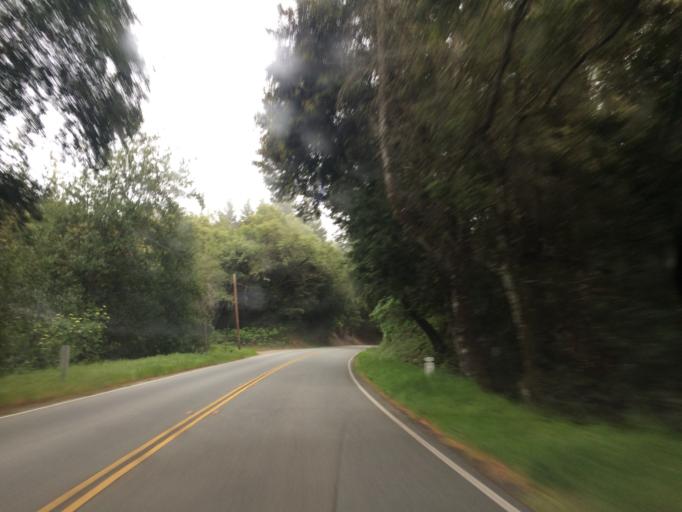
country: US
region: California
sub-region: Santa Clara County
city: Loyola
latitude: 37.2691
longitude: -122.1404
